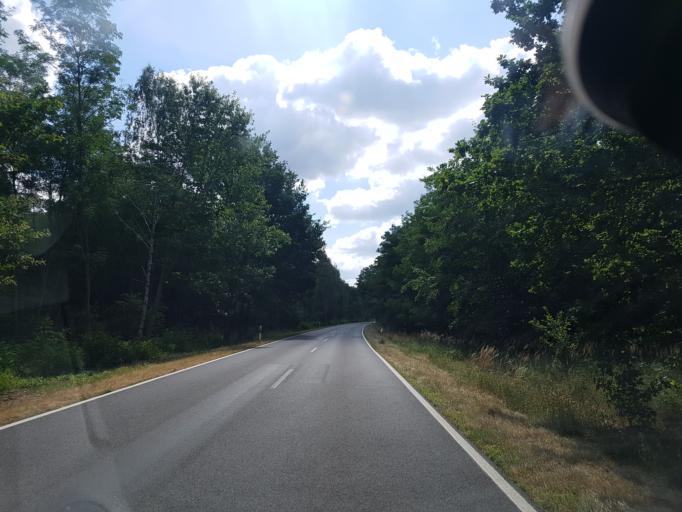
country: DE
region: Brandenburg
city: Neupetershain
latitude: 51.6829
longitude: 14.1485
